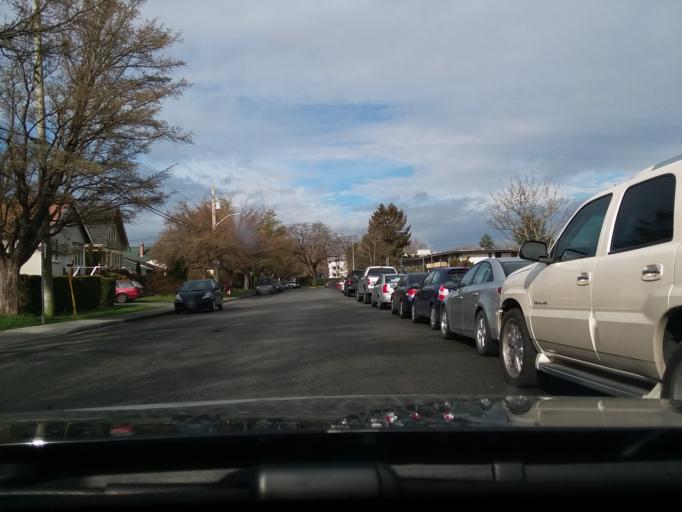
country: CA
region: British Columbia
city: Oak Bay
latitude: 48.4389
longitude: -123.3297
